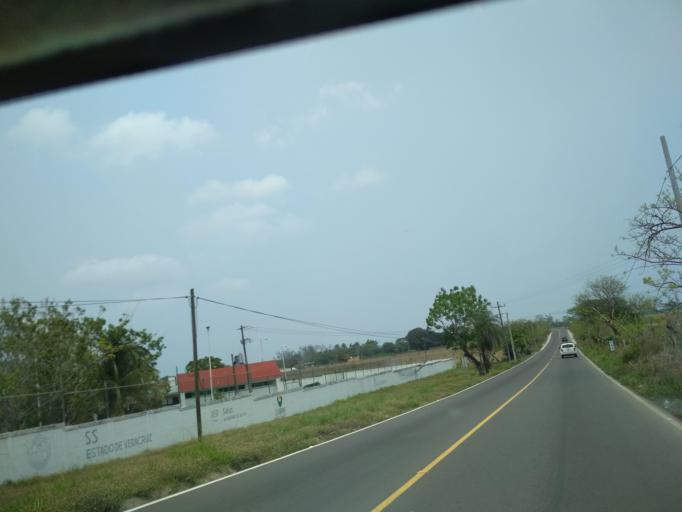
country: MX
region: Veracruz
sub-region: Veracruz
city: Delfino Victoria (Santa Fe)
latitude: 19.1736
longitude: -96.2739
